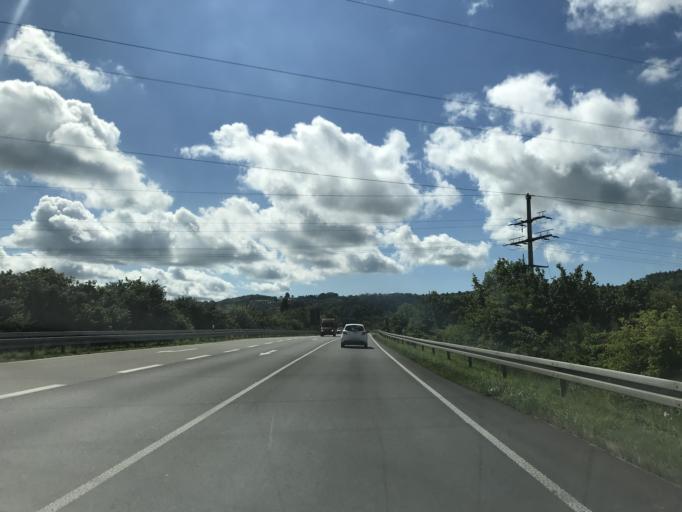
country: DE
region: Baden-Wuerttemberg
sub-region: Freiburg Region
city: Maulburg
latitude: 47.6462
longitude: 7.7944
